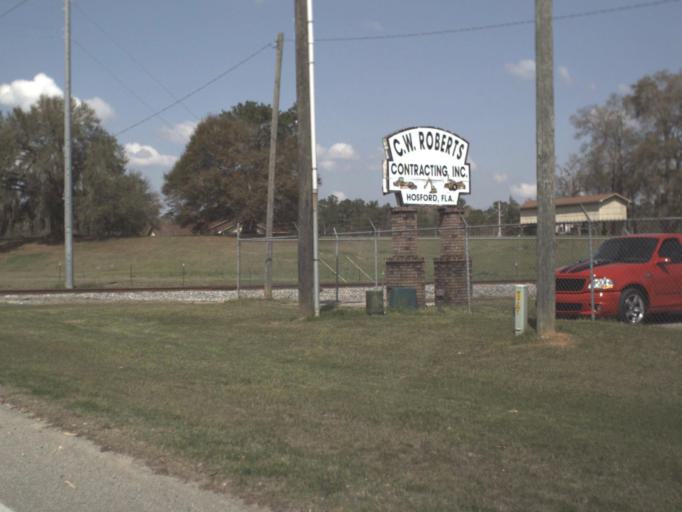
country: US
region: Florida
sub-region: Liberty County
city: Bristol
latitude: 30.3893
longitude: -84.7928
